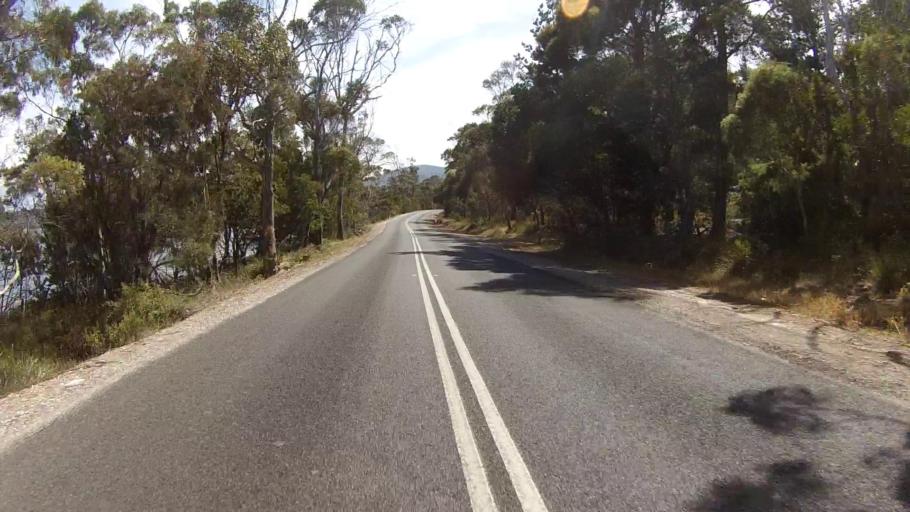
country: AU
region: Tasmania
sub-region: Huon Valley
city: Cygnet
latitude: -43.2648
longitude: 147.1428
